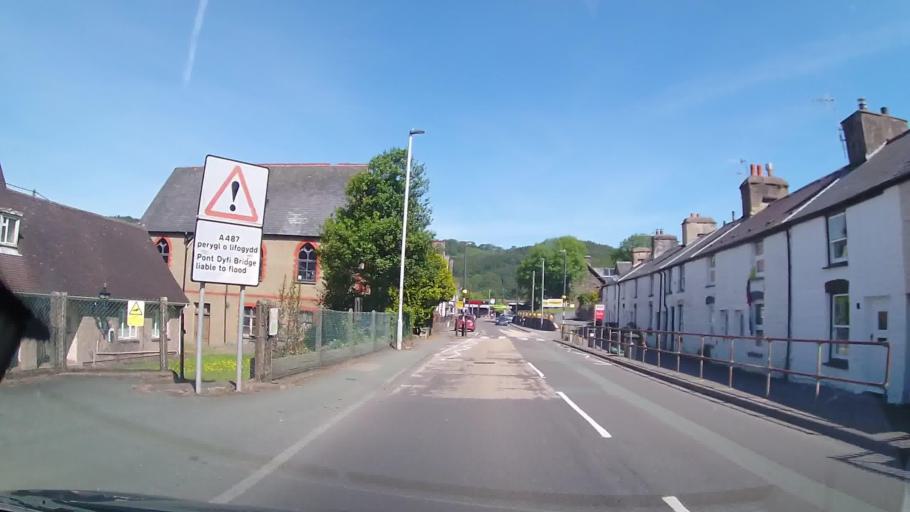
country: GB
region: Wales
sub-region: Sir Powys
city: Machynlleth
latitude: 52.5930
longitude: -3.8543
